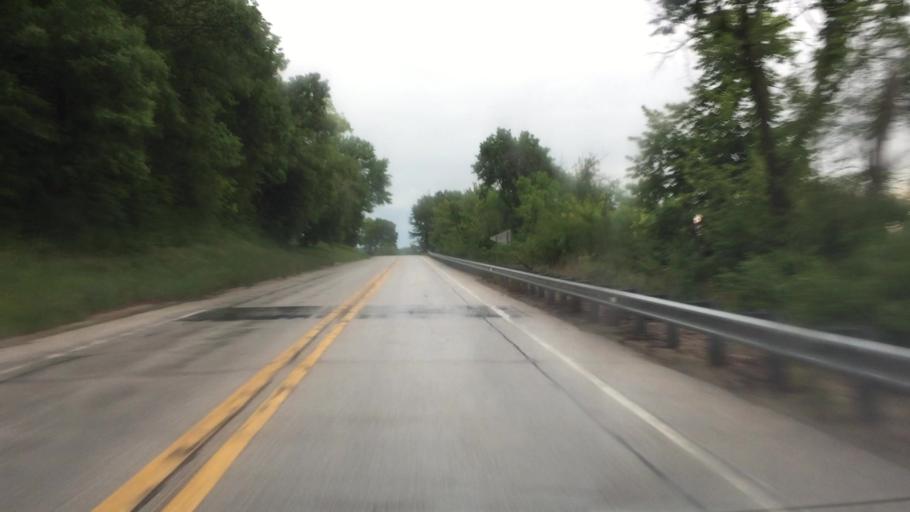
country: US
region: Iowa
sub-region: Lee County
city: Keokuk
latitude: 40.4361
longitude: -91.3709
